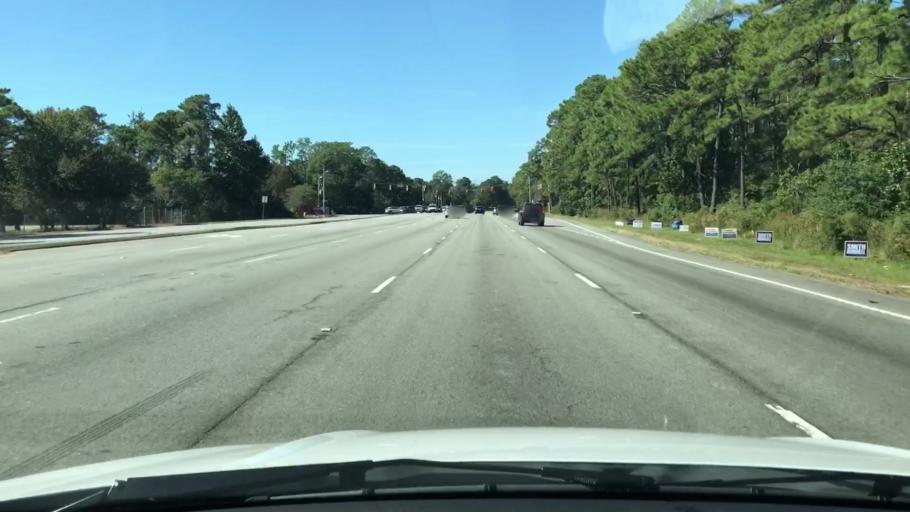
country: US
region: South Carolina
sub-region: Beaufort County
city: Bluffton
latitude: 32.2509
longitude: -80.8407
